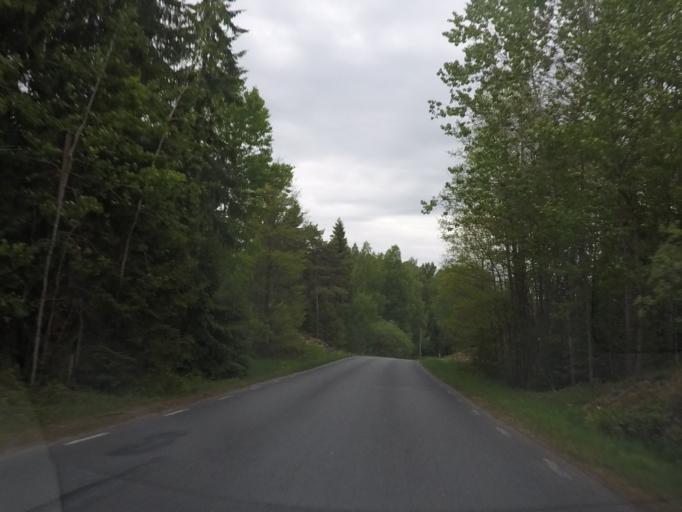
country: SE
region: Soedermanland
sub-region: Eskilstuna Kommun
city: Arla
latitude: 59.2620
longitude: 16.6547
